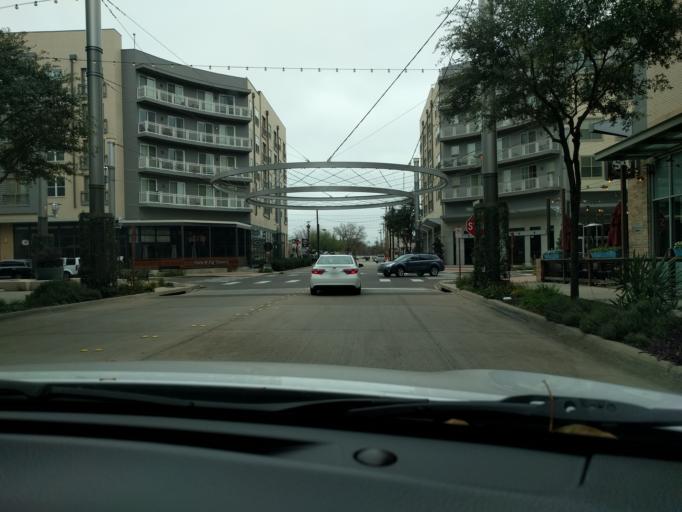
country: US
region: Texas
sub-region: Tarrant County
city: River Oaks
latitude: 32.7505
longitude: -97.3584
